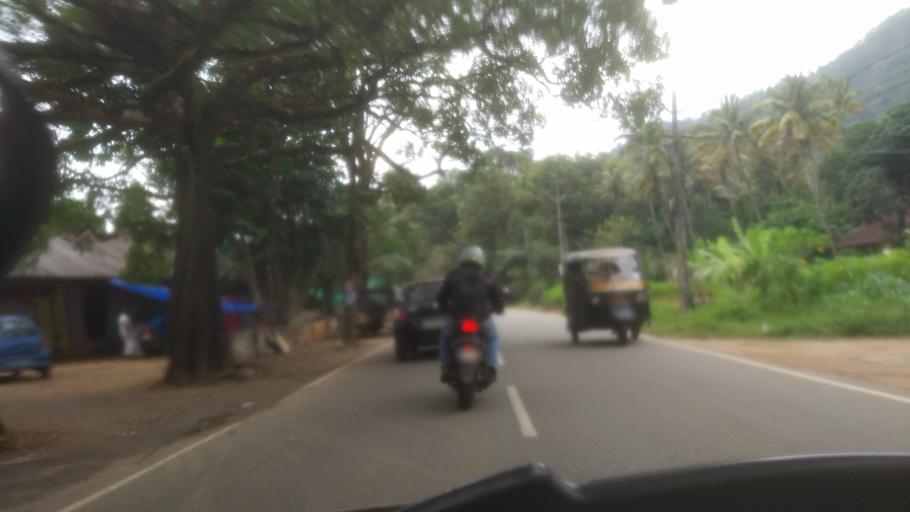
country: IN
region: Kerala
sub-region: Idukki
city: Munnar
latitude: 9.9894
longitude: 76.9838
